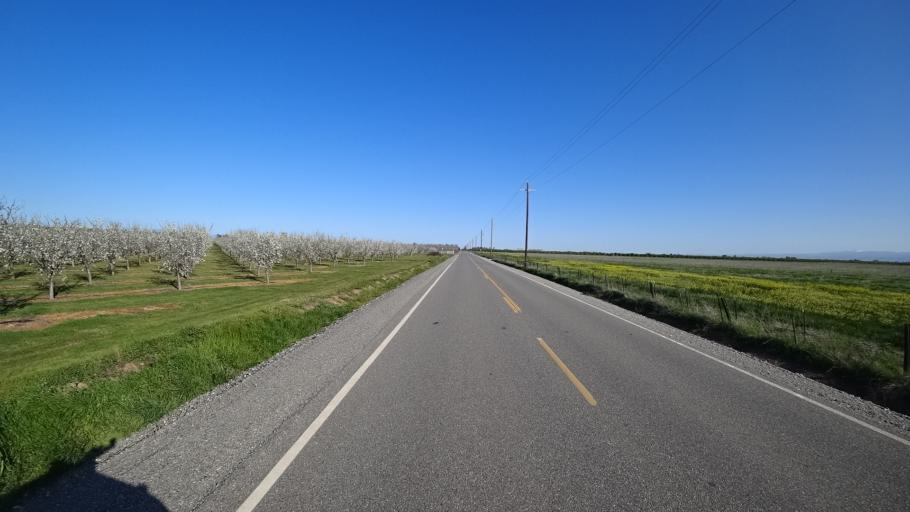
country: US
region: California
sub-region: Glenn County
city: Hamilton City
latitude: 39.7559
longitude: -122.1032
